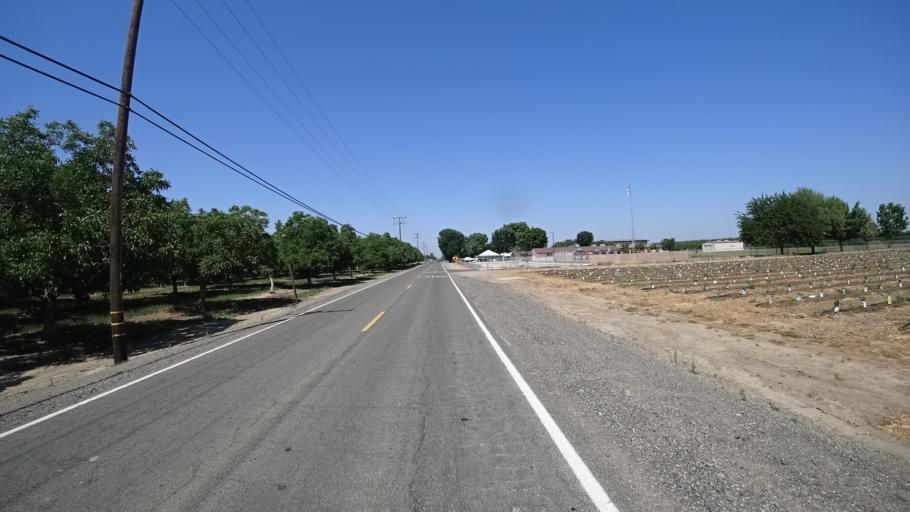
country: US
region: California
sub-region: Kings County
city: Lucerne
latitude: 36.3718
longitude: -119.6701
